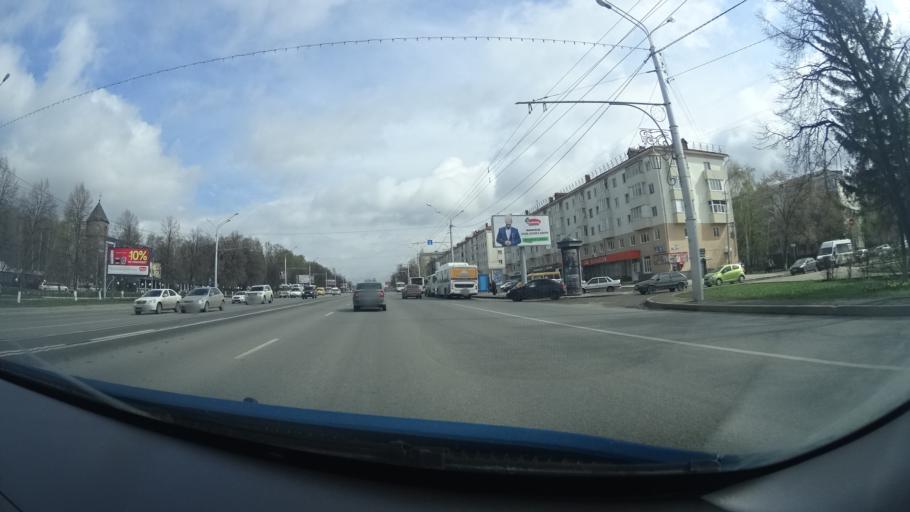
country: RU
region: Bashkortostan
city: Ufa
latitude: 54.7670
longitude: 56.0194
